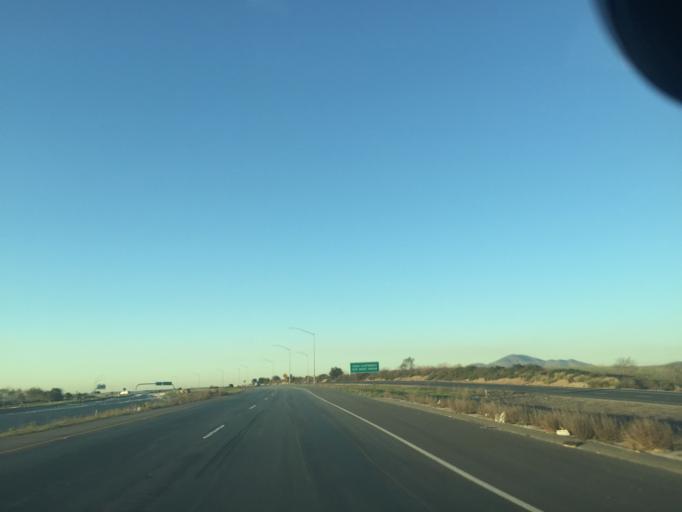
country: MX
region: Baja California
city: Tijuana
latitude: 32.5688
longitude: -116.9489
